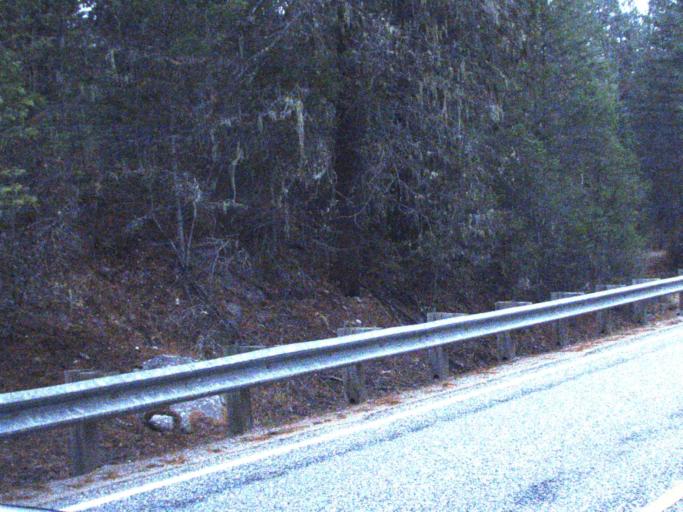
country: CA
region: British Columbia
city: Grand Forks
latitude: 48.9578
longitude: -118.2142
